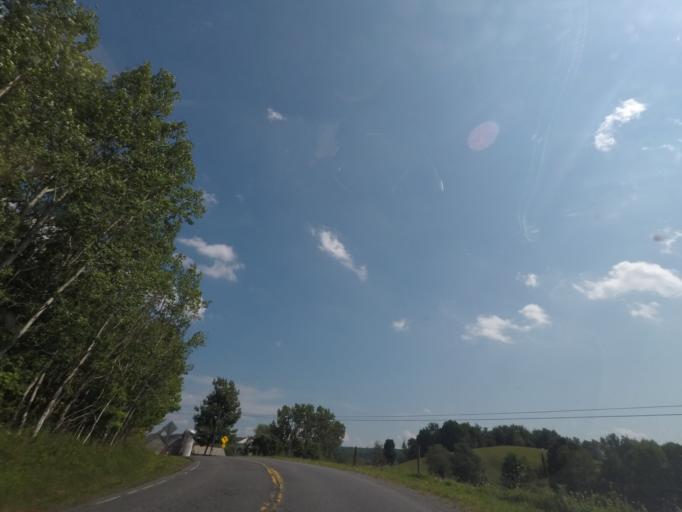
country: US
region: New York
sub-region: Saratoga County
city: Waterford
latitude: 42.8077
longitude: -73.5912
